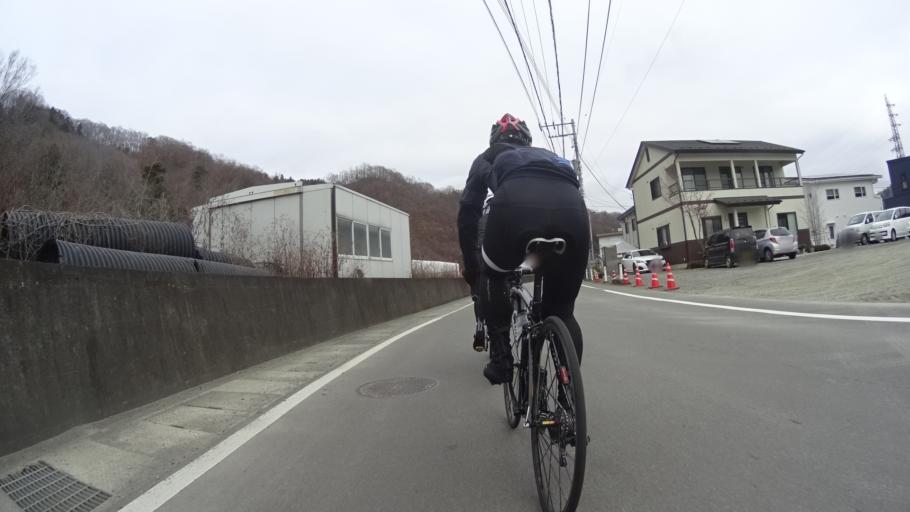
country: JP
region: Yamanashi
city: Otsuki
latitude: 35.5984
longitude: 138.9286
